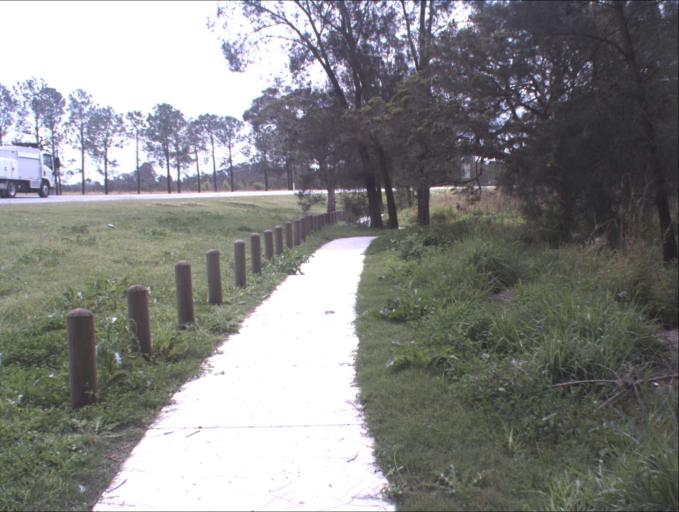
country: AU
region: Queensland
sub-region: Logan
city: Waterford West
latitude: -27.6973
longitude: 153.1180
